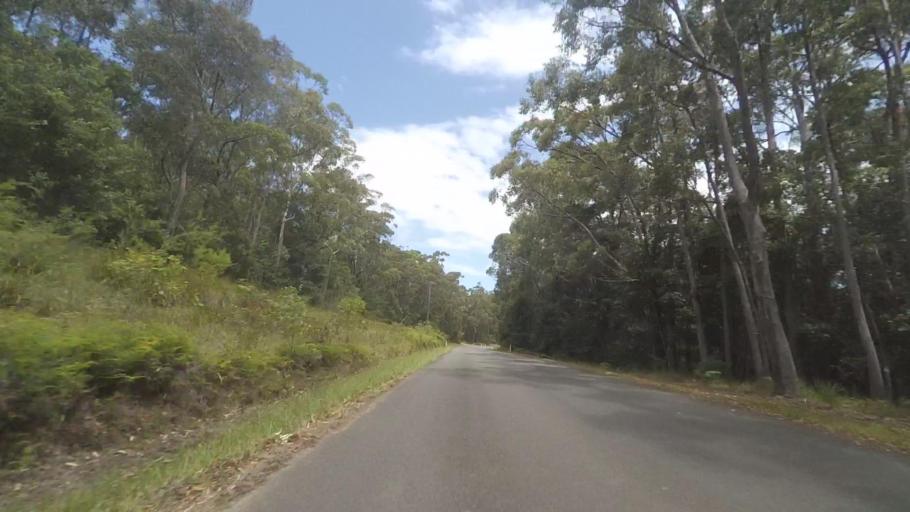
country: AU
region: New South Wales
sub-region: Shoalhaven Shire
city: Milton
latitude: -35.3872
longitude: 150.3664
